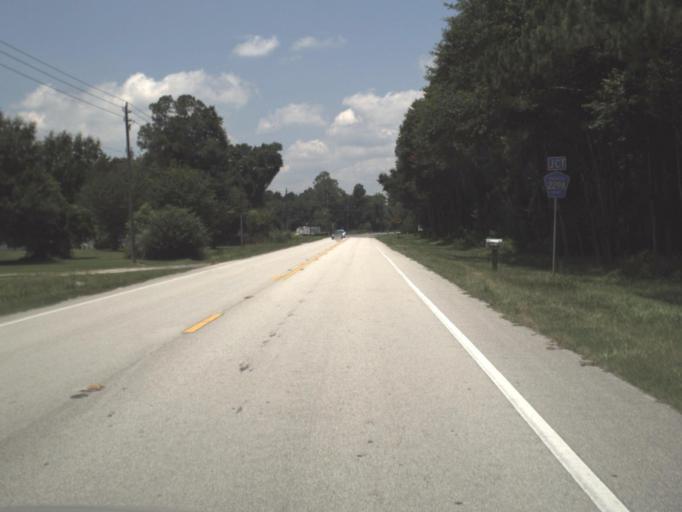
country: US
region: Florida
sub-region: Bradford County
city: Starke
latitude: 30.0177
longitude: -82.1486
